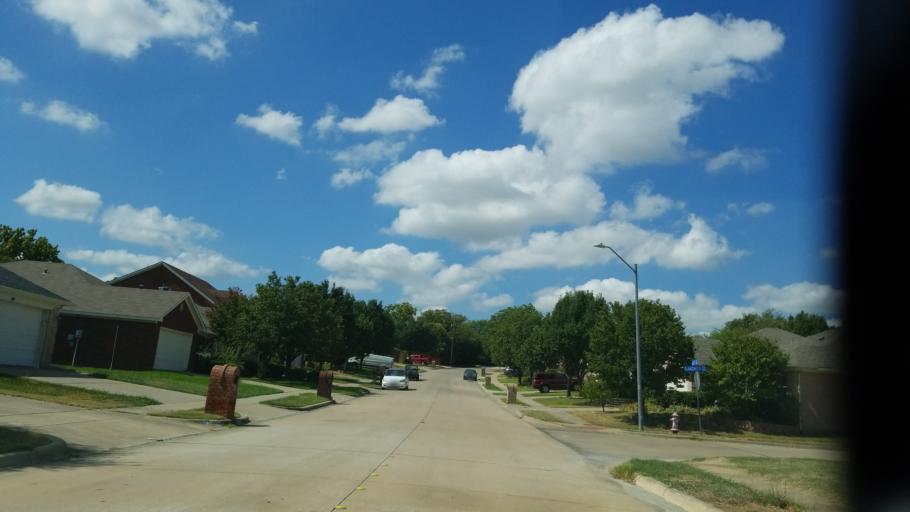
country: US
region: Texas
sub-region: Tarrant County
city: Euless
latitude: 32.8330
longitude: -97.0715
